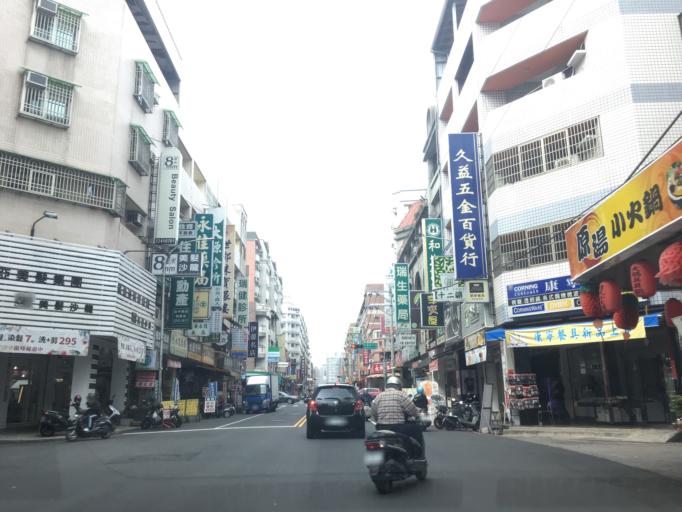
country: TW
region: Taiwan
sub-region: Taichung City
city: Taichung
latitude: 24.1739
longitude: 120.6945
